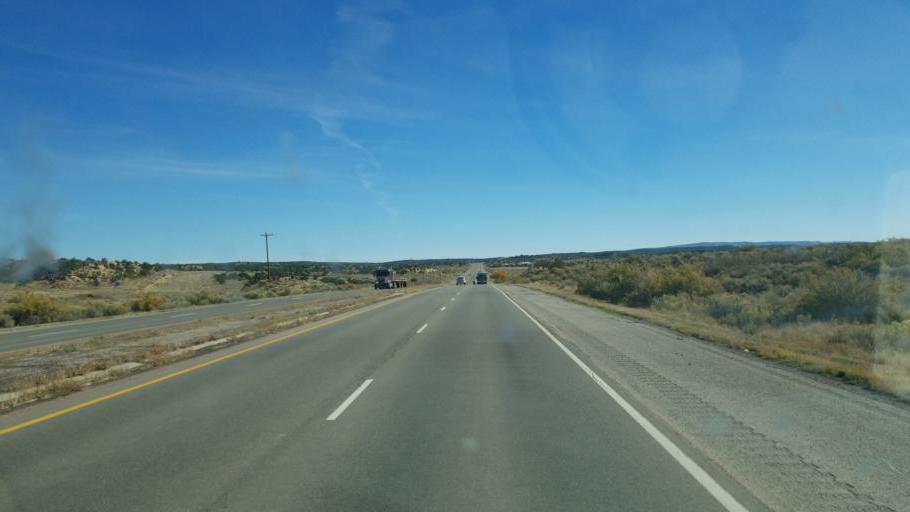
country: US
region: Arizona
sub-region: Apache County
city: Window Rock
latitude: 35.6281
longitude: -108.9289
